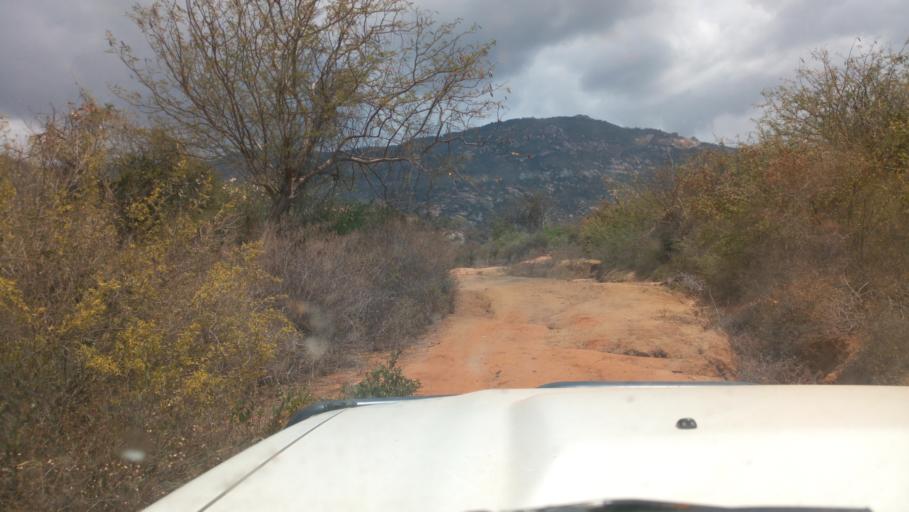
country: KE
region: Kitui
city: Kitui
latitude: -1.8838
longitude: 38.3750
